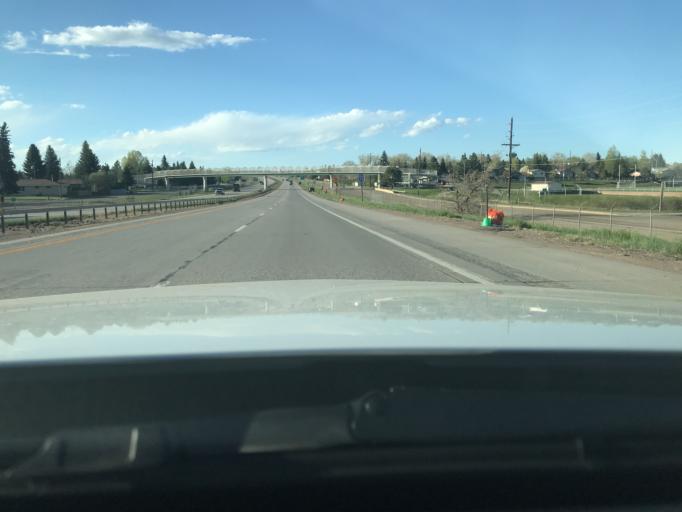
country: US
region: Wyoming
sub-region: Laramie County
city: Cheyenne
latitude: 41.1724
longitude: -104.8391
